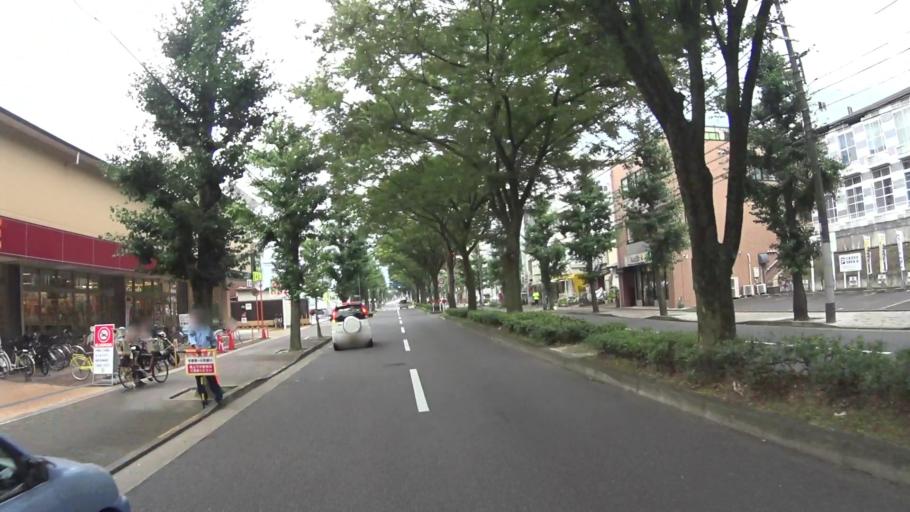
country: JP
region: Kyoto
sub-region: Kyoto-shi
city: Kamigyo-ku
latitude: 35.0376
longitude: 135.7919
